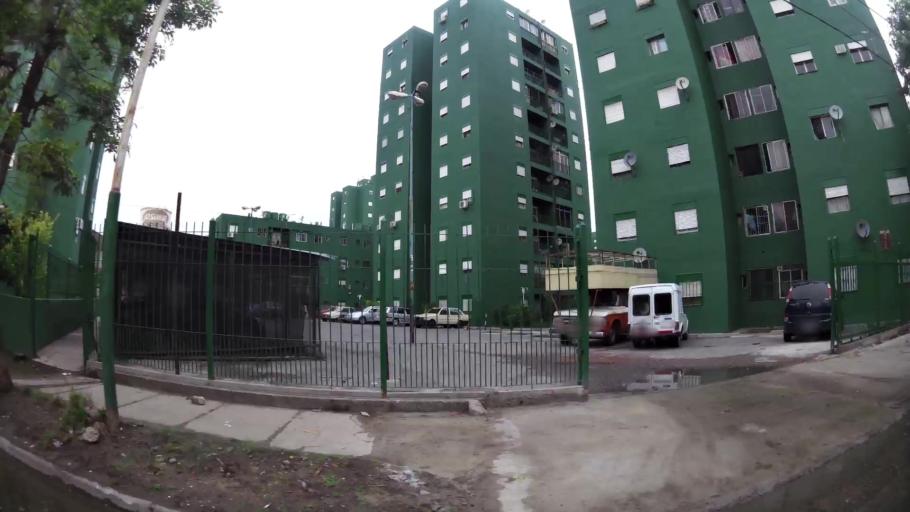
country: AR
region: Buenos Aires
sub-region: Partido de Lanus
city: Lanus
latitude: -34.7090
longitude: -58.3572
